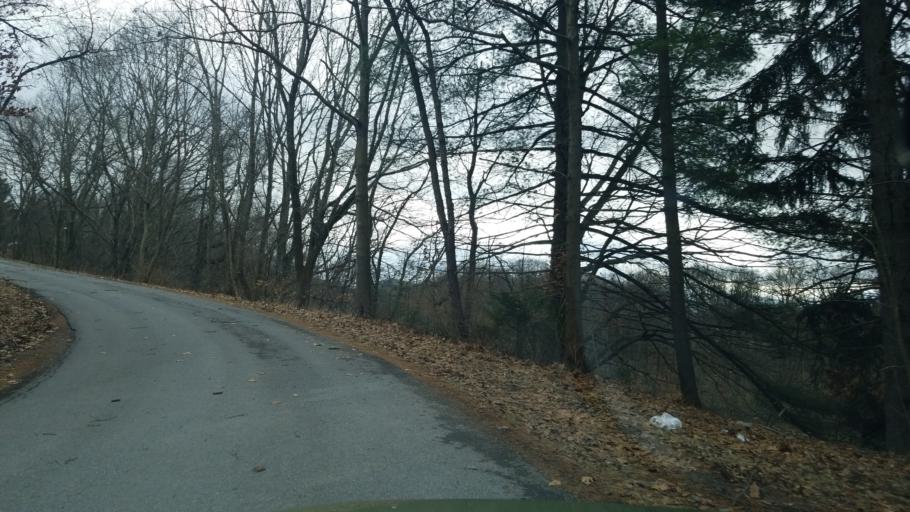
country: US
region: Pennsylvania
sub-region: Clearfield County
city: Clearfield
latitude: 41.0292
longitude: -78.4074
